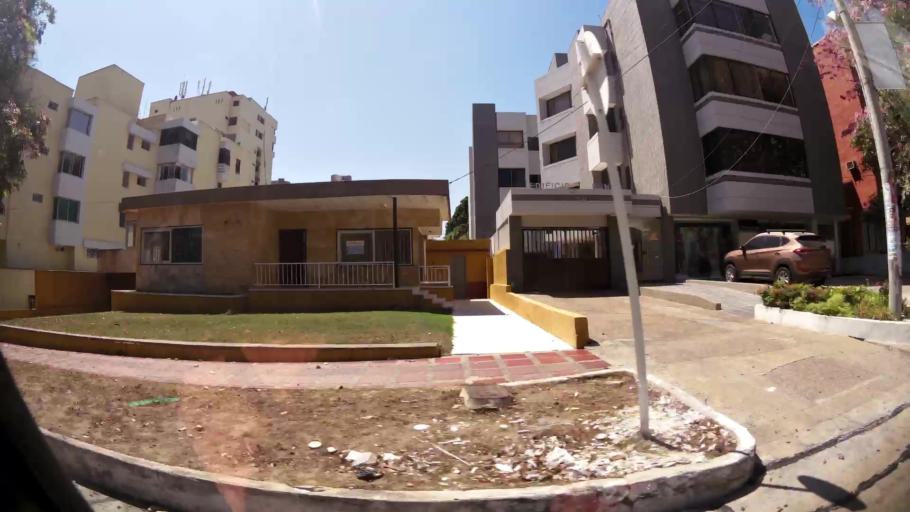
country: CO
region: Atlantico
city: Barranquilla
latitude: 11.0047
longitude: -74.8151
